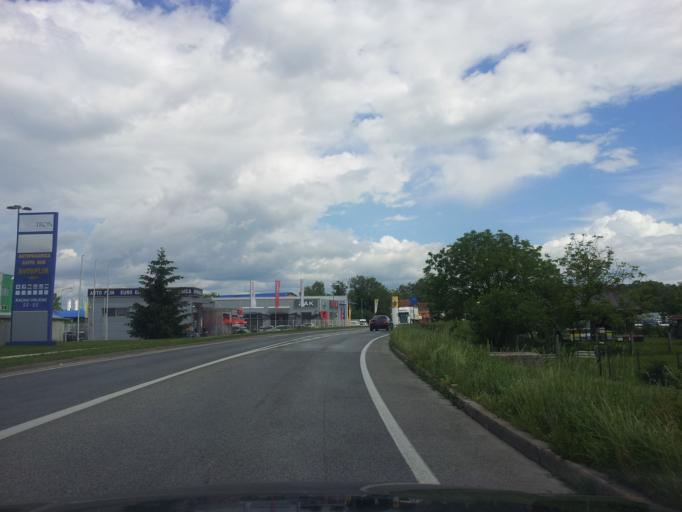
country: HR
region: Karlovacka
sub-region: Grad Karlovac
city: Karlovac
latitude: 45.5168
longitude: 15.5443
